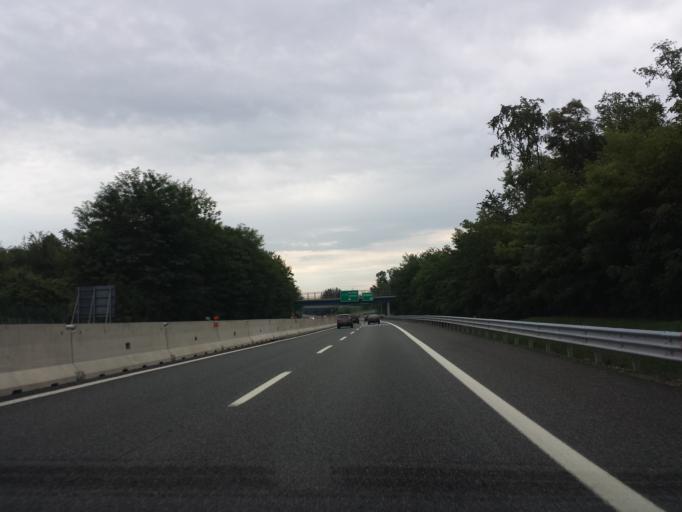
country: IT
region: Lombardy
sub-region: Provincia di Varese
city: Besnate
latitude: 45.6953
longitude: 8.7527
